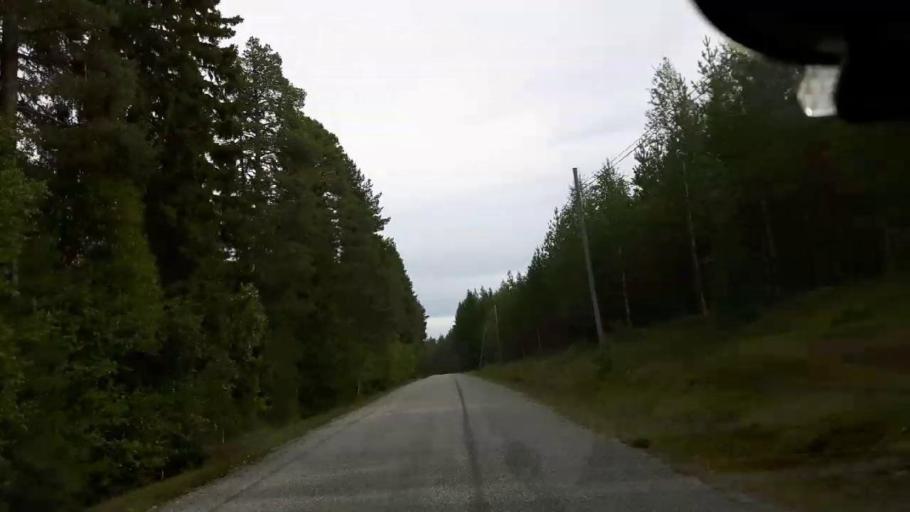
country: SE
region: Jaemtland
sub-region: Ragunda Kommun
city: Hammarstrand
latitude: 63.0113
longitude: 16.1049
